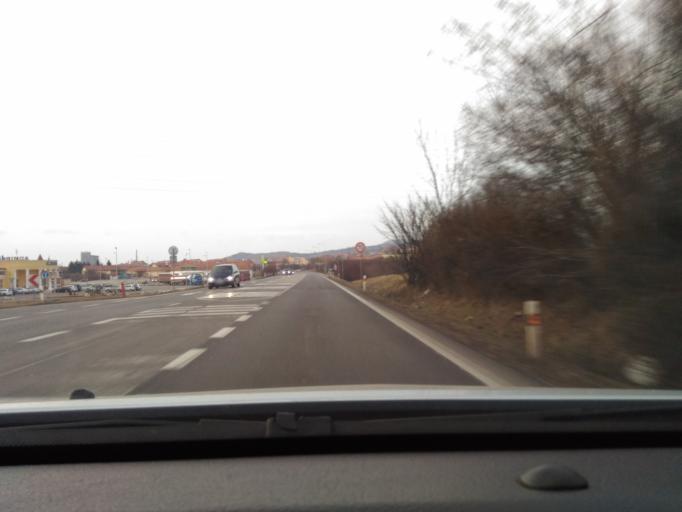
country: CZ
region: South Moravian
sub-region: Okres Breclav
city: Mikulov
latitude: 48.7958
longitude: 16.6333
